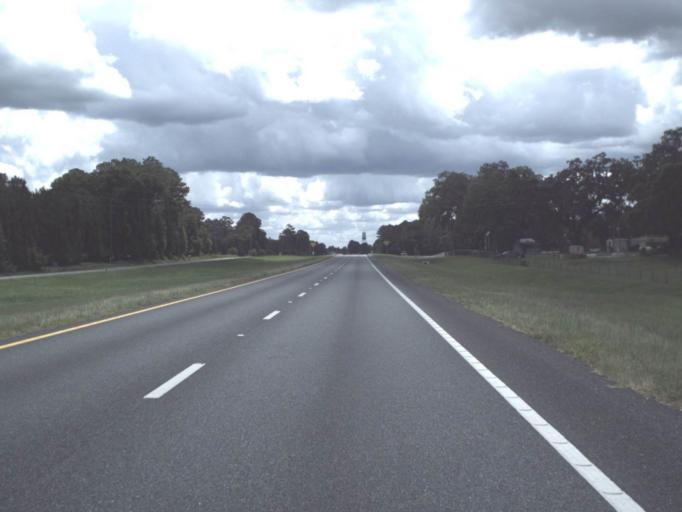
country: US
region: Florida
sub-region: Levy County
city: Williston
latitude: 29.3903
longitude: -82.4716
